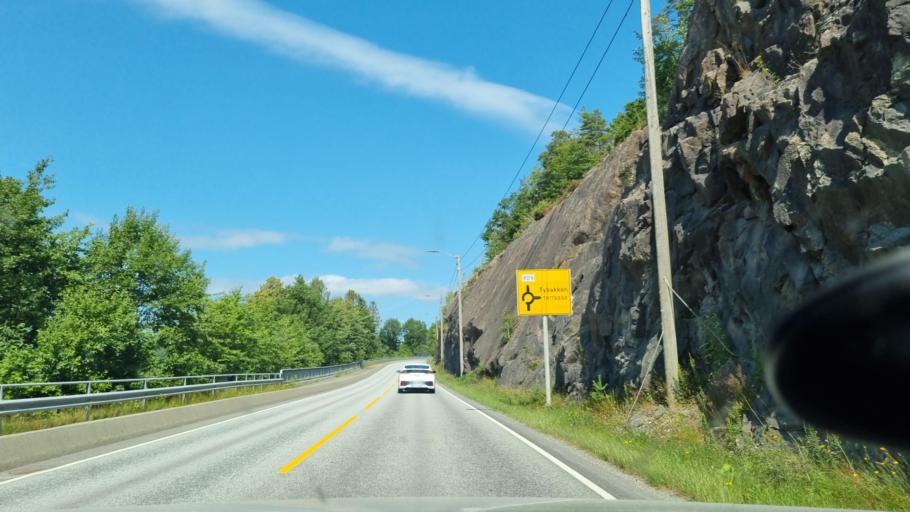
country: NO
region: Aust-Agder
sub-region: Arendal
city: Arendal
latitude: 58.4610
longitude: 8.8194
